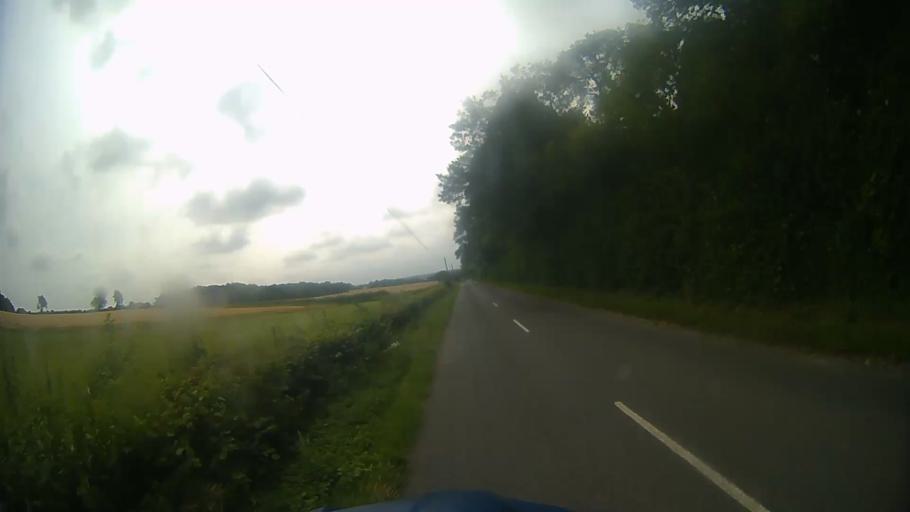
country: GB
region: England
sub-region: Hampshire
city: Overton
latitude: 51.2730
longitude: -1.2993
